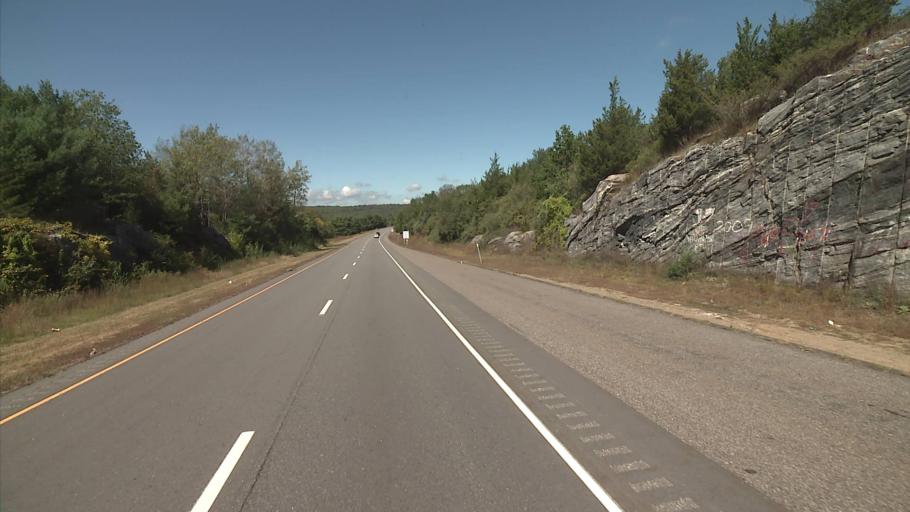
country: US
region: Connecticut
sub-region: New London County
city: Colchester
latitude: 41.4678
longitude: -72.2831
